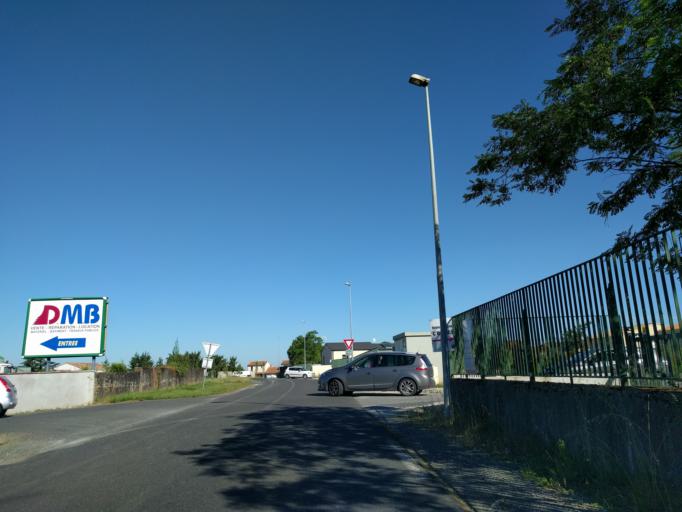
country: FR
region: Poitou-Charentes
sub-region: Departement des Deux-Sevres
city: Chauray
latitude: 46.3392
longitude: -0.4164
